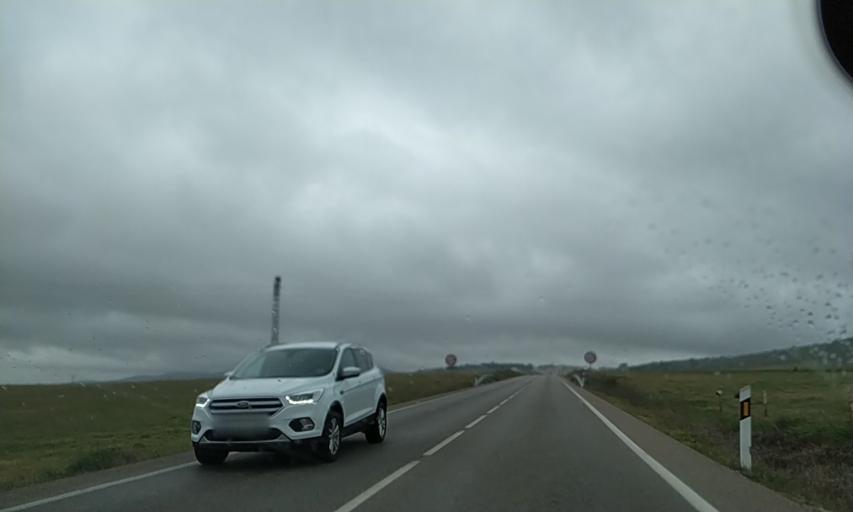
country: ES
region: Extremadura
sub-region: Provincia de Caceres
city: Caceres
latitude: 39.5024
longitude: -6.3895
